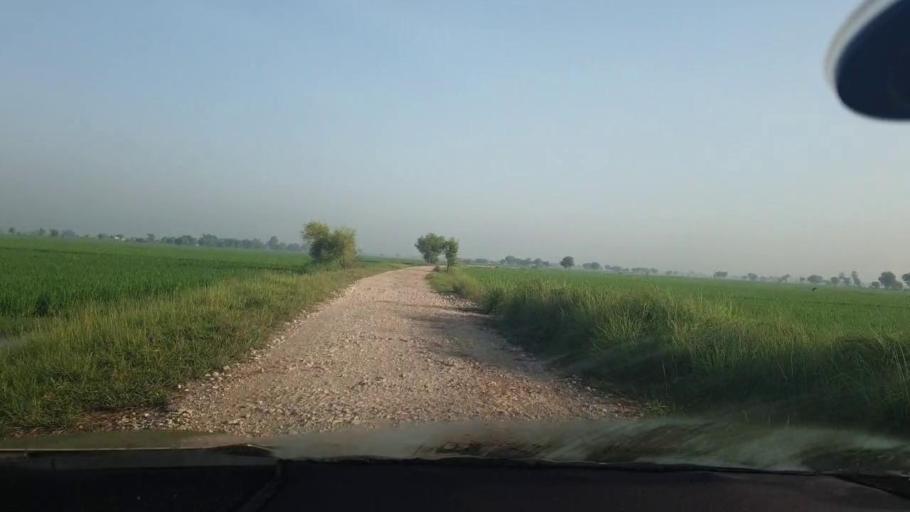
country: PK
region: Sindh
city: Kambar
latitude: 27.6231
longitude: 68.0178
